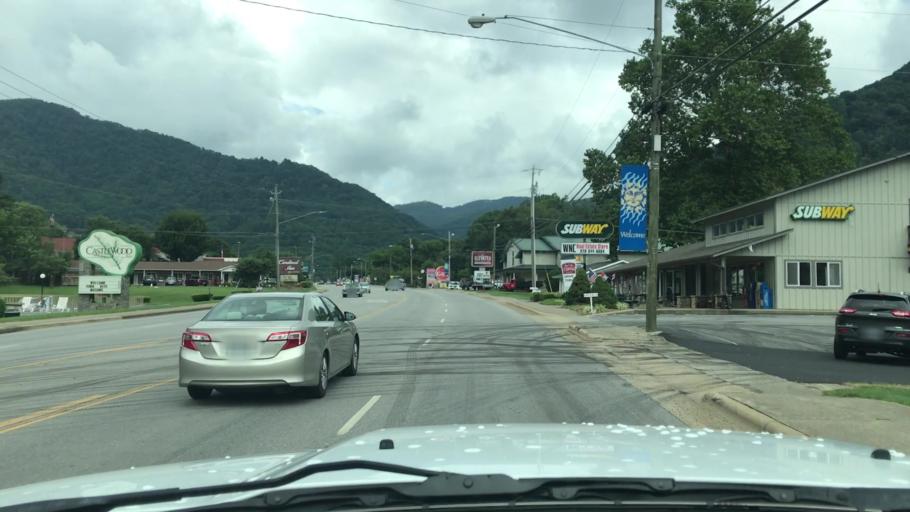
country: US
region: North Carolina
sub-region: Haywood County
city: Maggie Valley
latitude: 35.5174
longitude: -83.0889
